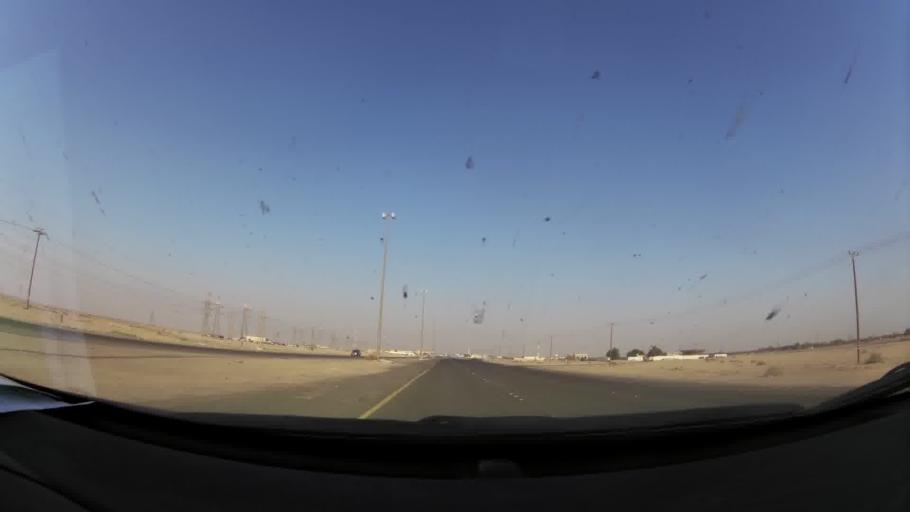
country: IQ
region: Basra Governorate
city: Umm Qasr
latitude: 30.0721
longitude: 47.6917
